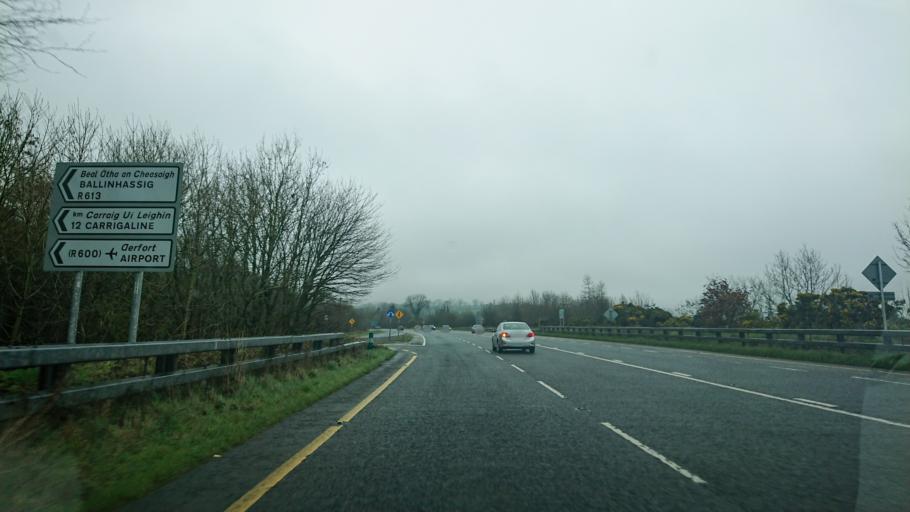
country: IE
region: Munster
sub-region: County Cork
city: Kinsale
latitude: 51.8121
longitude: -8.5380
